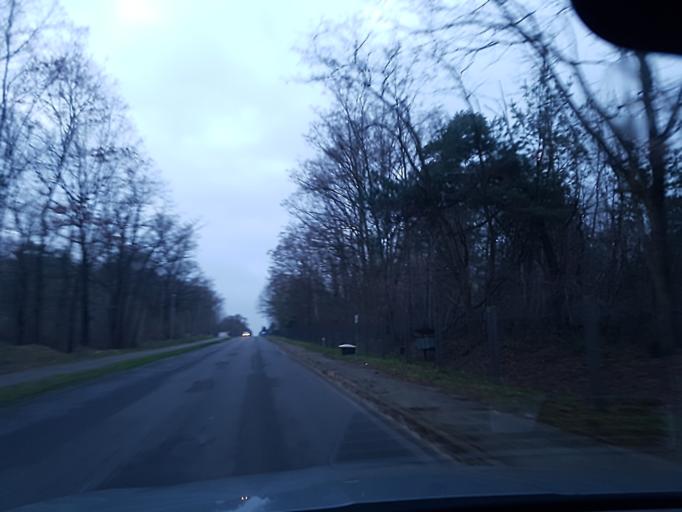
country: DE
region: Brandenburg
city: Schonborn
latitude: 51.6009
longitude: 13.4832
